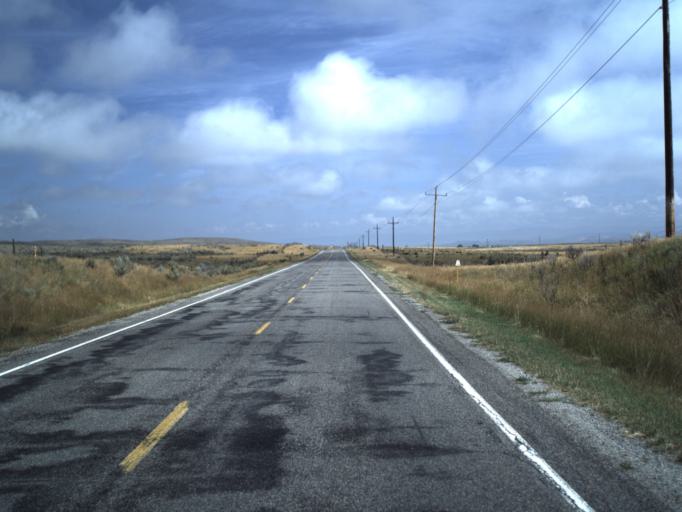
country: US
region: Utah
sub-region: Rich County
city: Randolph
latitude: 41.7428
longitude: -111.1524
